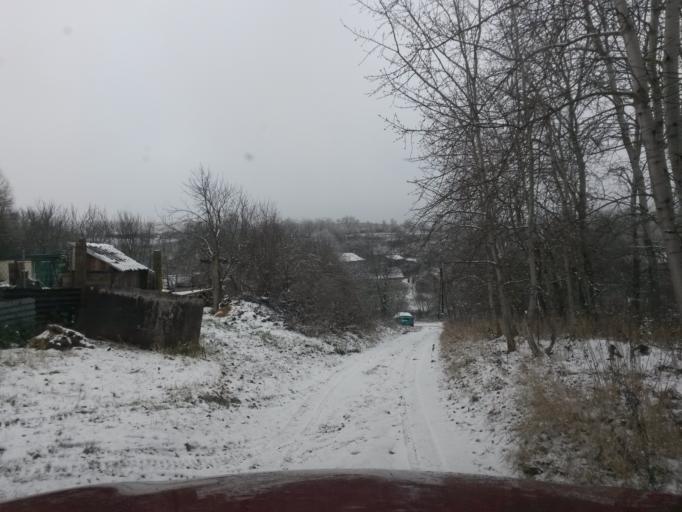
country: SK
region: Presovsky
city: Sabinov
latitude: 48.9881
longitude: 21.0796
